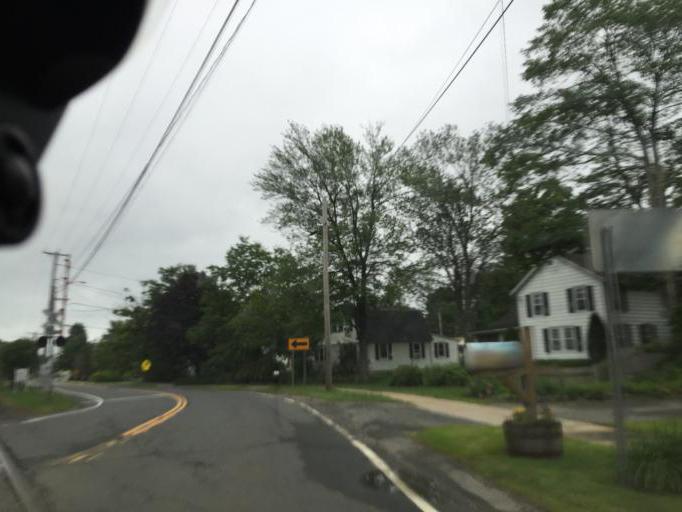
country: US
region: Connecticut
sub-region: Litchfield County
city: Canaan
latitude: 42.0326
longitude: -73.3274
